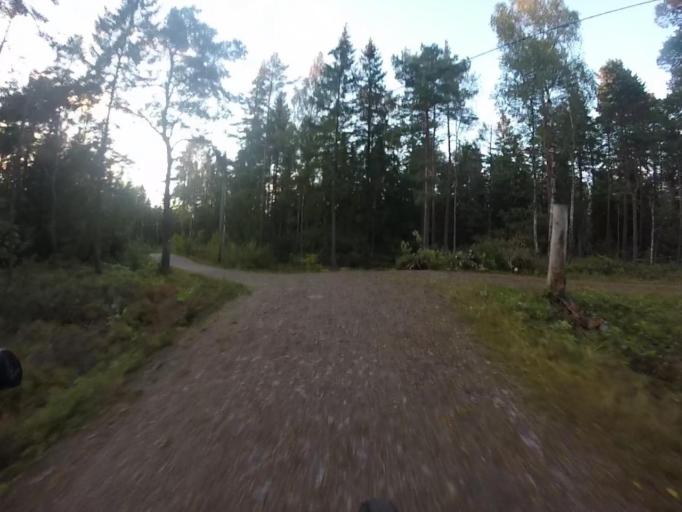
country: SE
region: Vaestra Goetaland
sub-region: Trollhattan
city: Trollhattan
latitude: 58.2969
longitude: 12.2693
